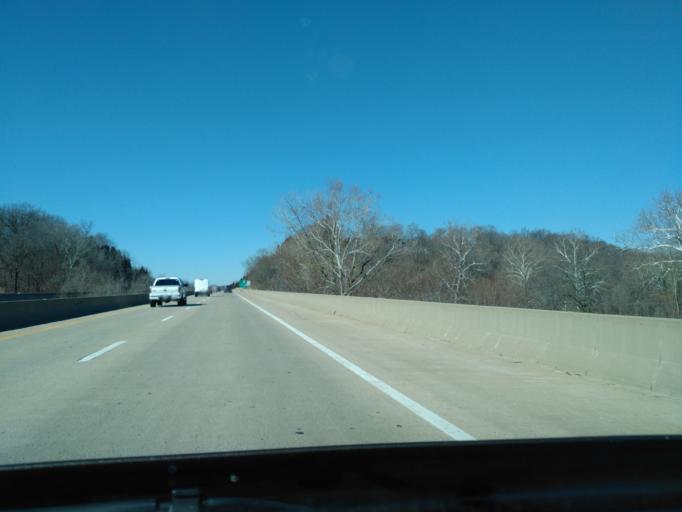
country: US
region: Missouri
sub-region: Saint Louis County
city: Fenton
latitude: 38.5161
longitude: -90.4356
